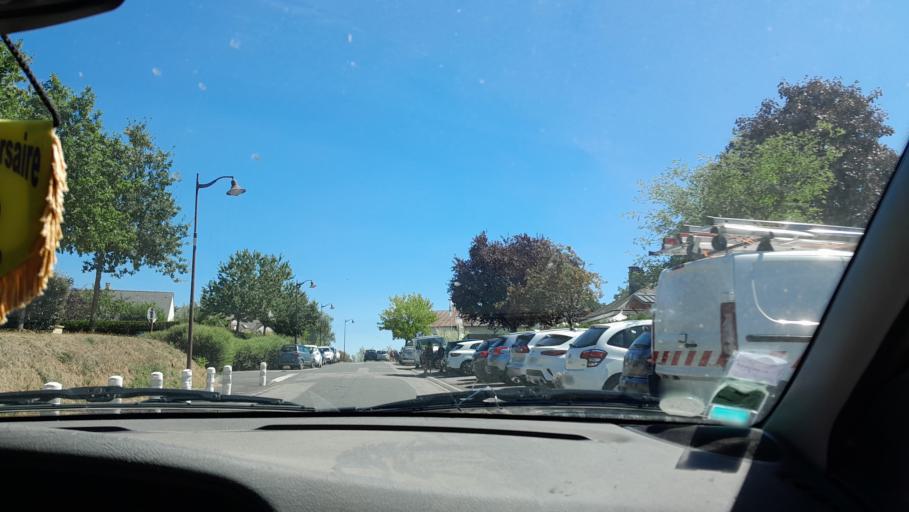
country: FR
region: Pays de la Loire
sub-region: Departement de Maine-et-Loire
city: Pouance
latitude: 47.7490
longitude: -1.1788
